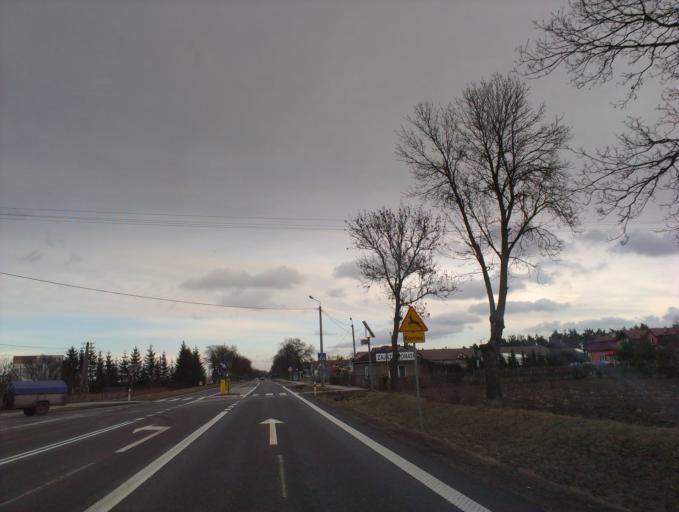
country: PL
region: Masovian Voivodeship
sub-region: Powiat sierpecki
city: Sierpc
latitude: 52.8702
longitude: 19.6450
